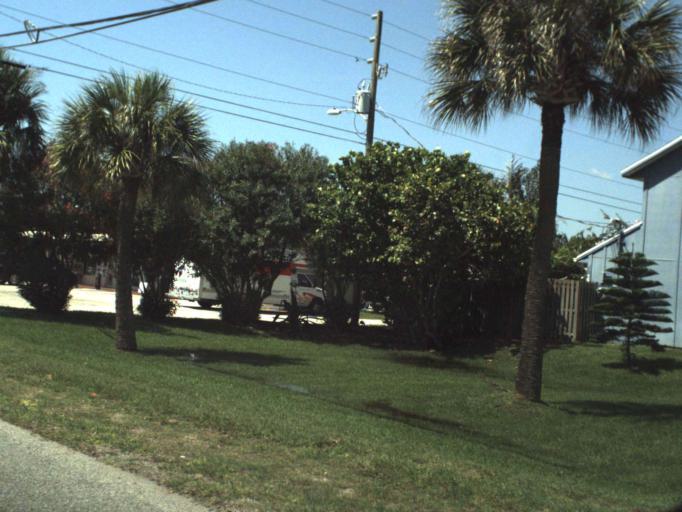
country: US
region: Florida
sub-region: Brevard County
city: Cocoa Beach
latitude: 28.2878
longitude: -80.6093
